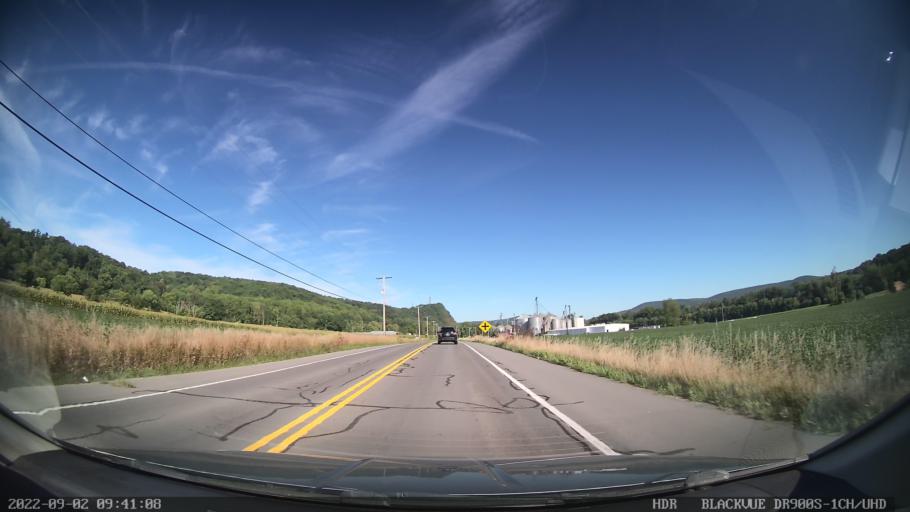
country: US
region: Pennsylvania
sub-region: Montour County
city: Danville
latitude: 40.9339
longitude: -76.5961
